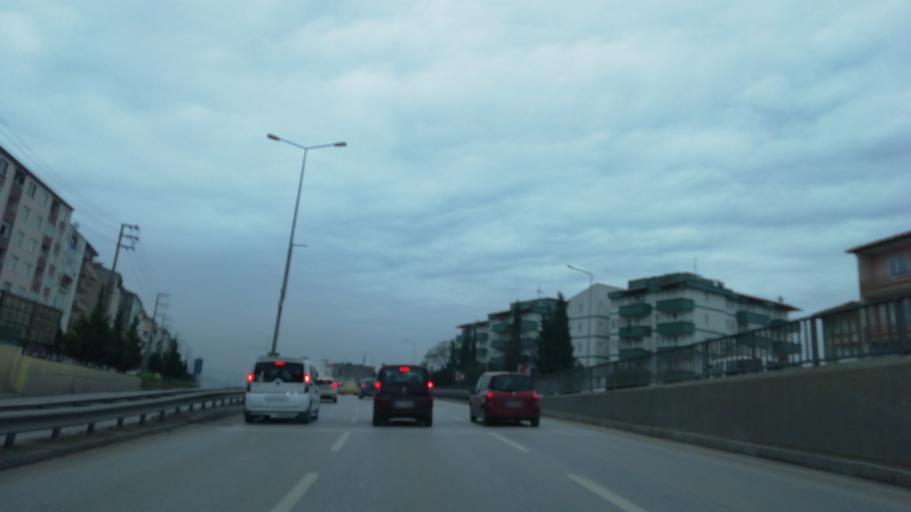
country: TR
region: Kocaeli
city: Derince
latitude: 40.7560
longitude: 29.8330
